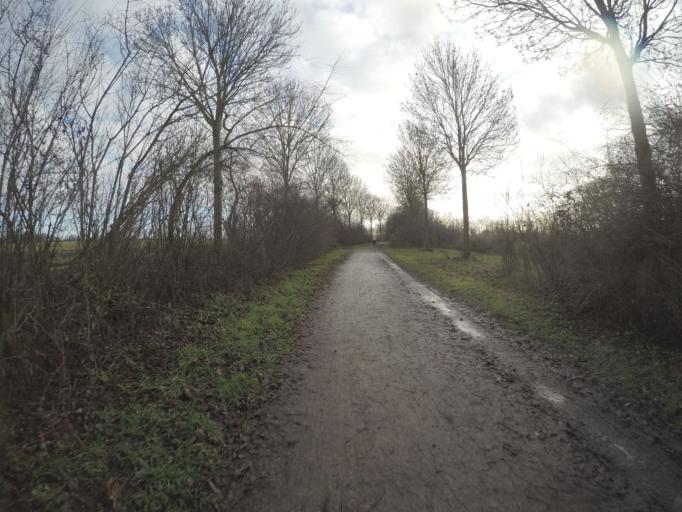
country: DE
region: Berlin
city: Wartenberg
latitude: 52.5921
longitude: 13.5187
